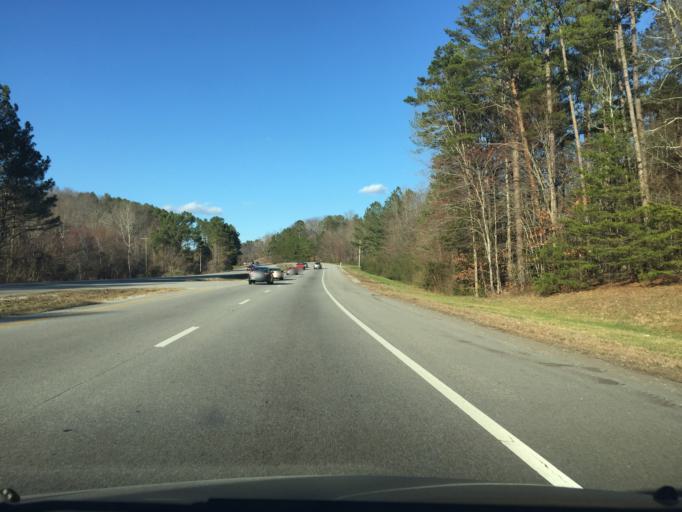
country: US
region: Tennessee
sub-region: Hamilton County
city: Harrison
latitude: 35.1293
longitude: -85.1241
